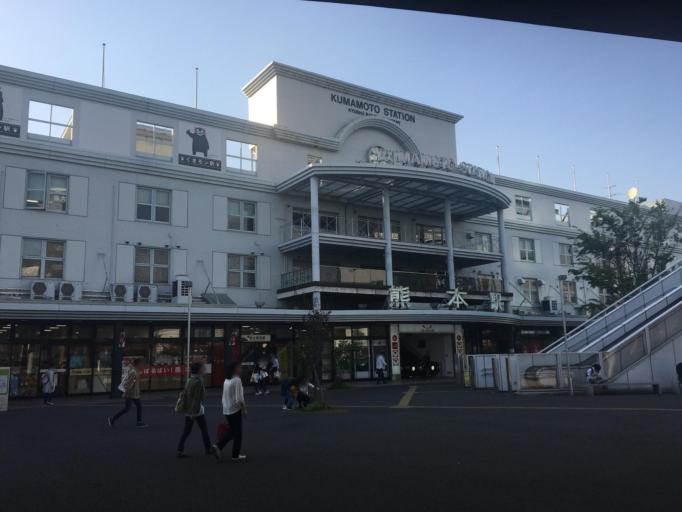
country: JP
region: Kumamoto
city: Kumamoto
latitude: 32.7898
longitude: 130.6896
